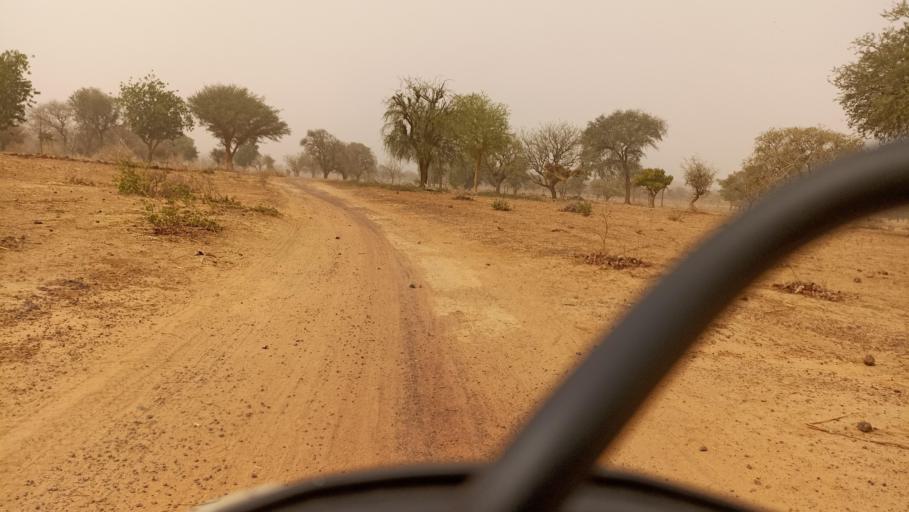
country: BF
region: Nord
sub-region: Province du Zondoma
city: Gourcy
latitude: 13.2743
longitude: -2.5371
